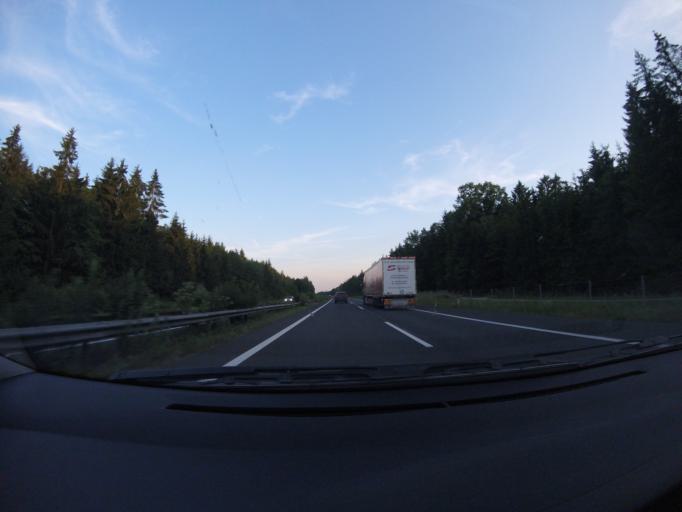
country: AT
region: Styria
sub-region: Politischer Bezirk Hartberg-Fuerstenfeld
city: Bad Waltersdorf
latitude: 47.1274
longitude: 15.9846
